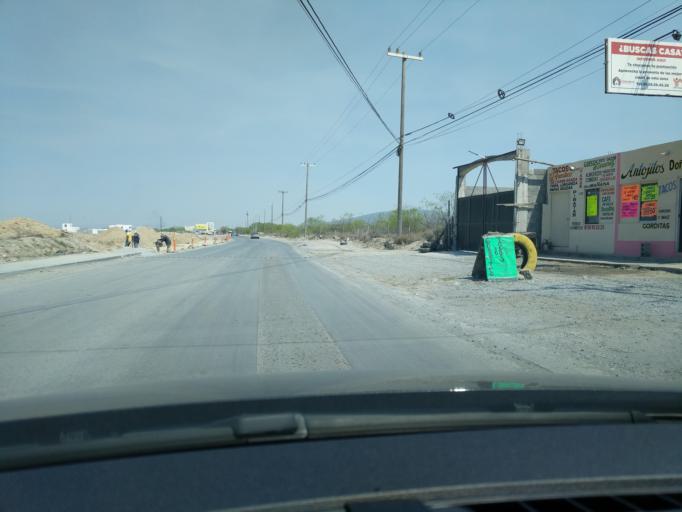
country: MX
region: Nuevo Leon
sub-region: Garcia
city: Valle de Lincoln
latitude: 25.7931
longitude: -100.4741
